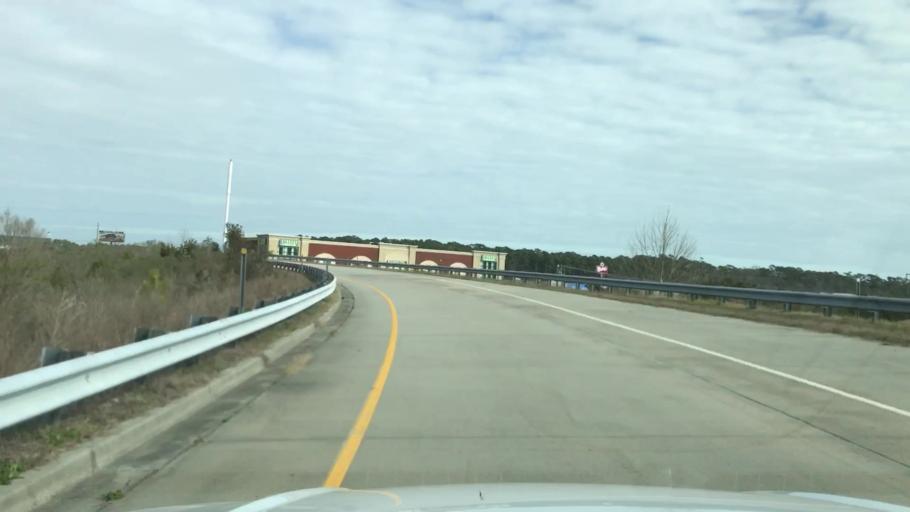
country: US
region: South Carolina
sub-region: Horry County
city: North Myrtle Beach
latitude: 33.7856
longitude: -78.7738
